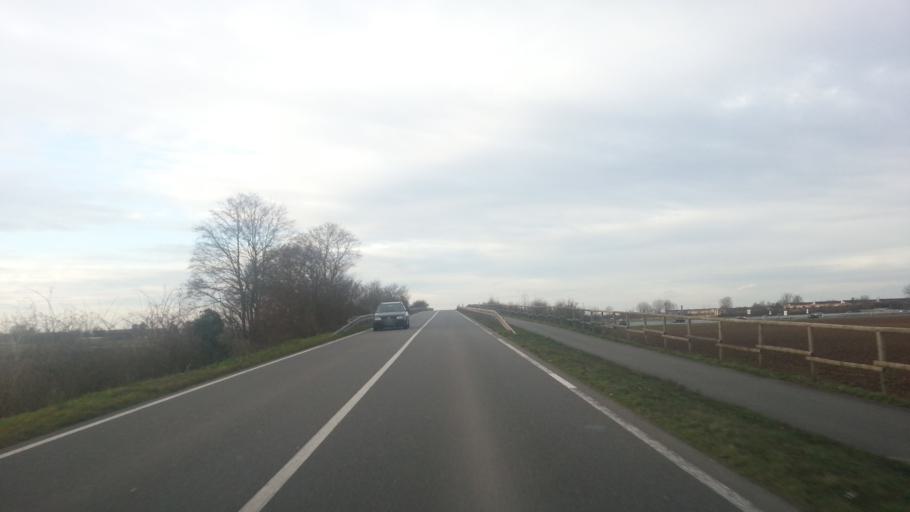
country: DE
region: Baden-Wuerttemberg
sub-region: Karlsruhe Region
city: Sandhausen
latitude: 49.3638
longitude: 8.6348
